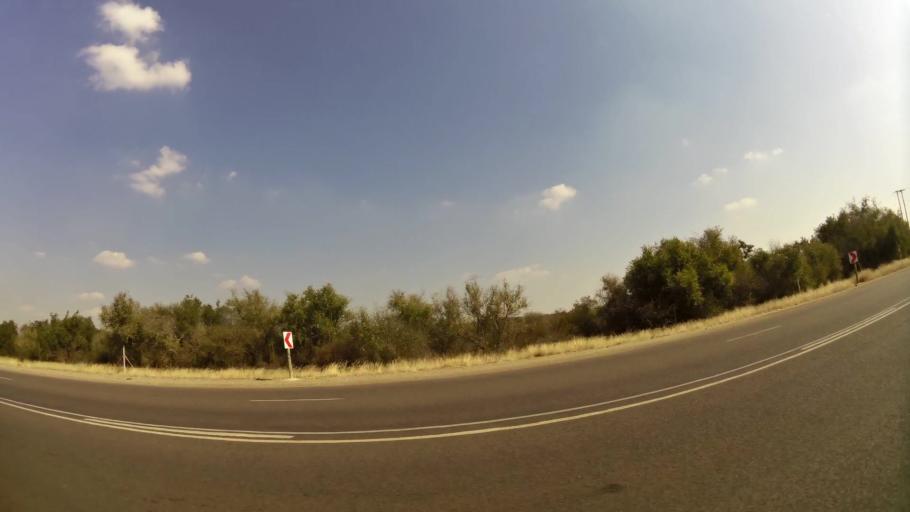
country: ZA
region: North-West
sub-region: Bojanala Platinum District Municipality
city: Mogwase
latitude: -25.4346
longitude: 27.0839
